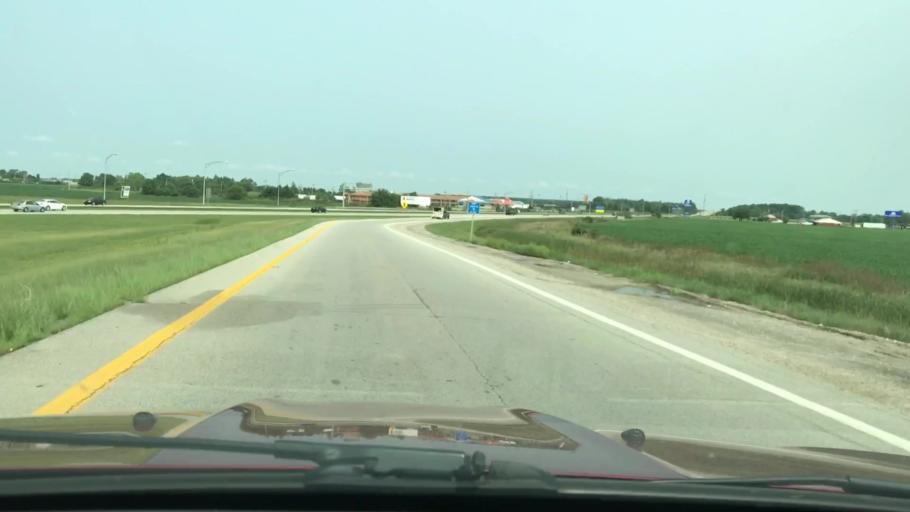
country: US
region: Ohio
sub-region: Wood County
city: Millbury
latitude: 41.5373
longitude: -83.4618
